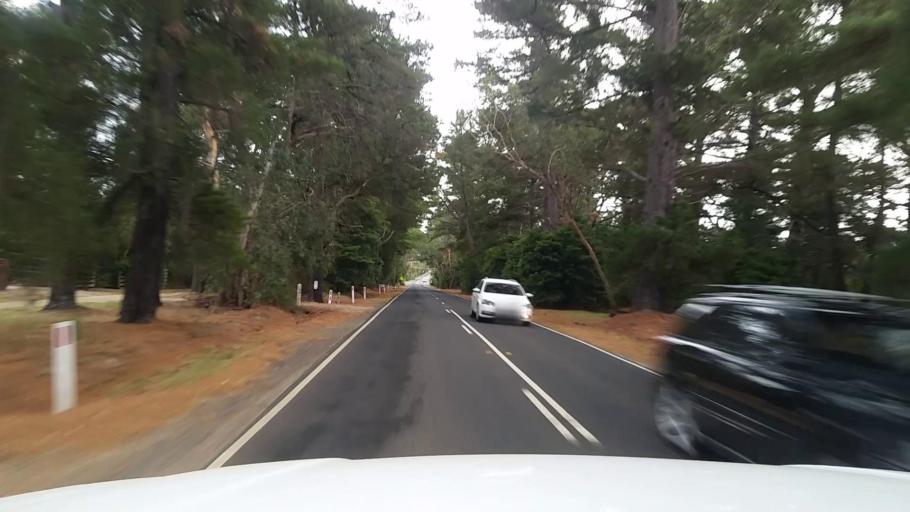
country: AU
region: Victoria
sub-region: Mornington Peninsula
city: Balnarring
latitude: -38.3658
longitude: 145.1190
